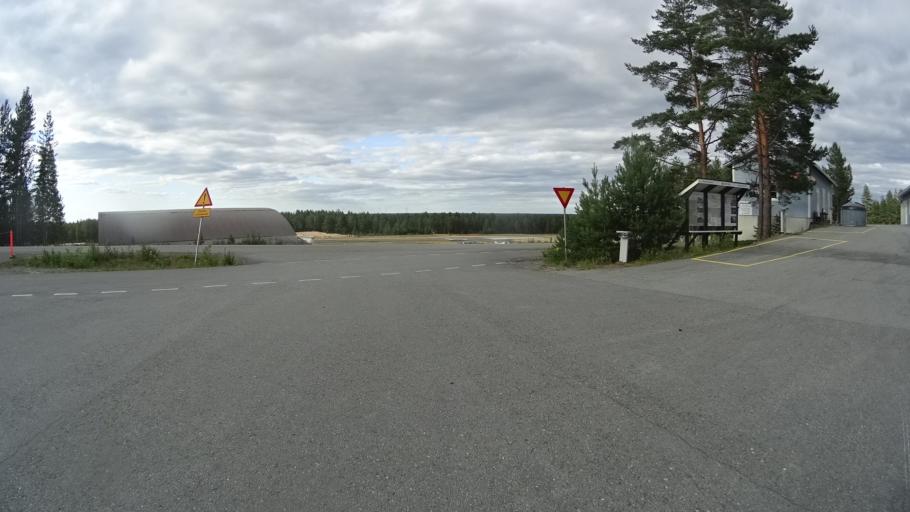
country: FI
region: Satakunta
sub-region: Pohjois-Satakunta
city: Jaemijaervi
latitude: 61.7793
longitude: 22.7158
